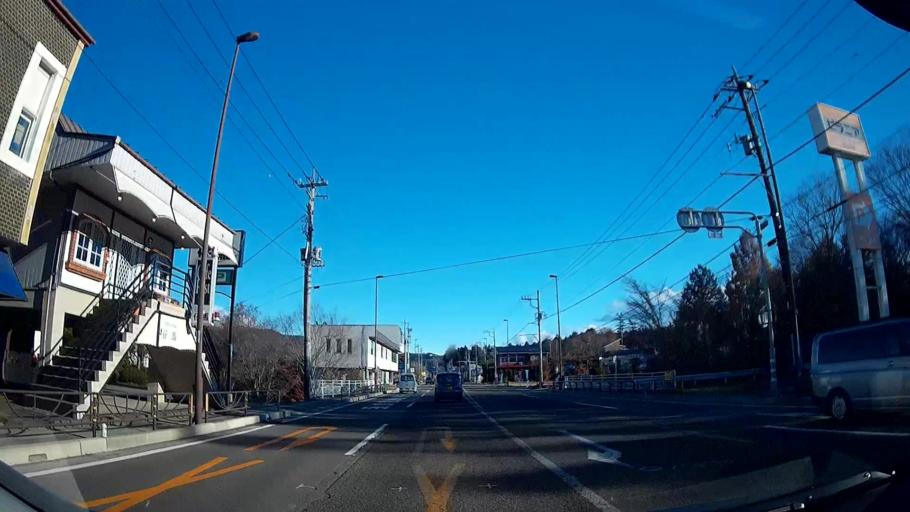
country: JP
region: Yamanashi
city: Fujikawaguchiko
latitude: 35.4766
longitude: 138.7892
